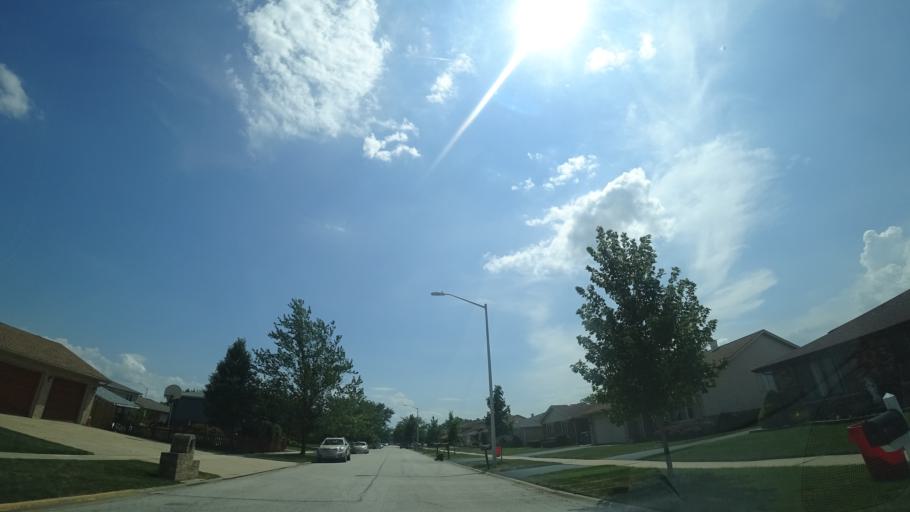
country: US
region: Illinois
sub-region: Cook County
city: Crestwood
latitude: 41.6751
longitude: -87.7519
